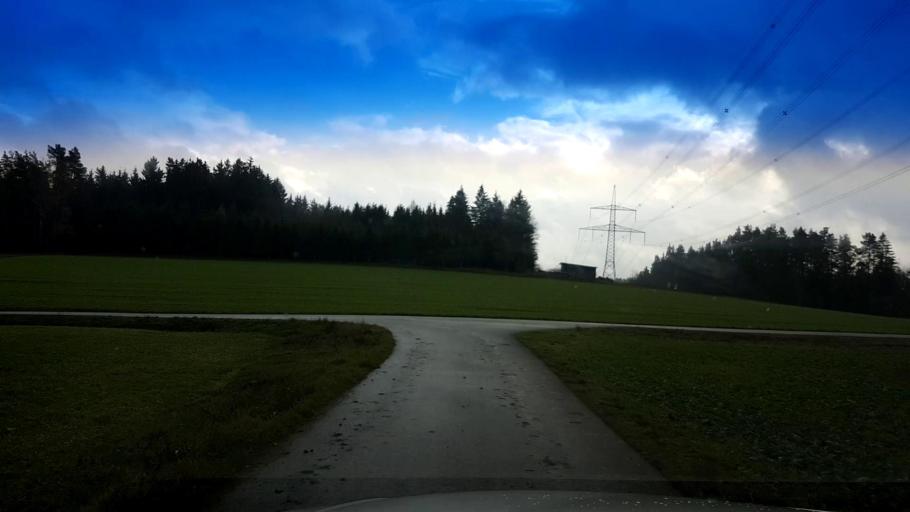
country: DE
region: Bavaria
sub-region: Upper Franconia
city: Poxdorf
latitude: 49.9322
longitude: 11.1058
